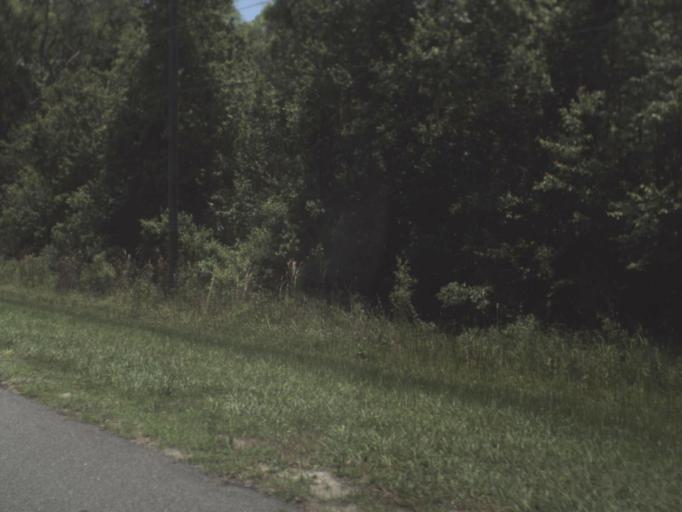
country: US
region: Florida
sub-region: Suwannee County
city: Wellborn
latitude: 30.2424
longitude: -82.8652
